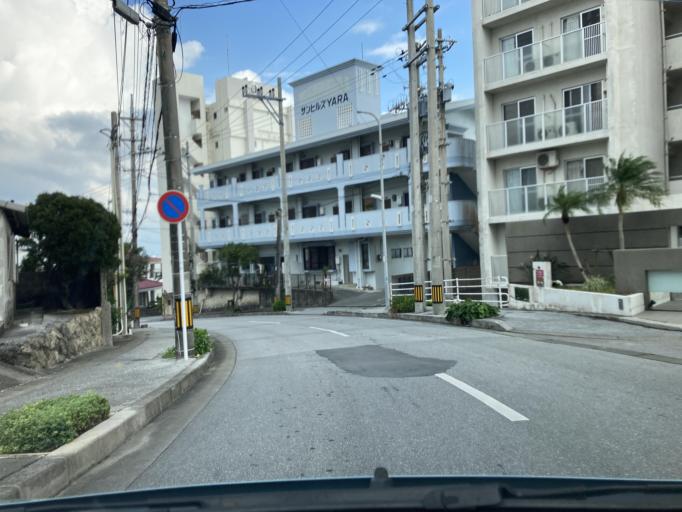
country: JP
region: Okinawa
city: Ginowan
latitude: 26.2402
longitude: 127.7623
